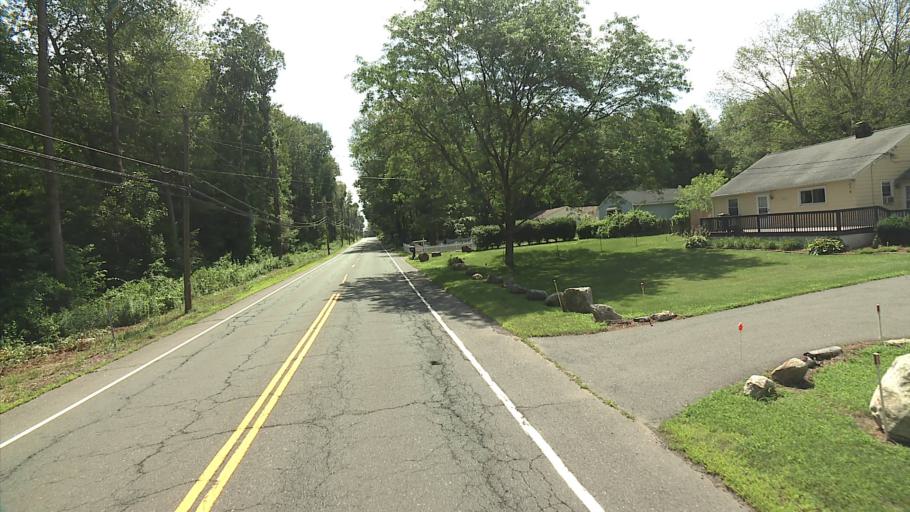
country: US
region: Connecticut
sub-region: Tolland County
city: Coventry Lake
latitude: 41.7877
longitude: -72.3420
